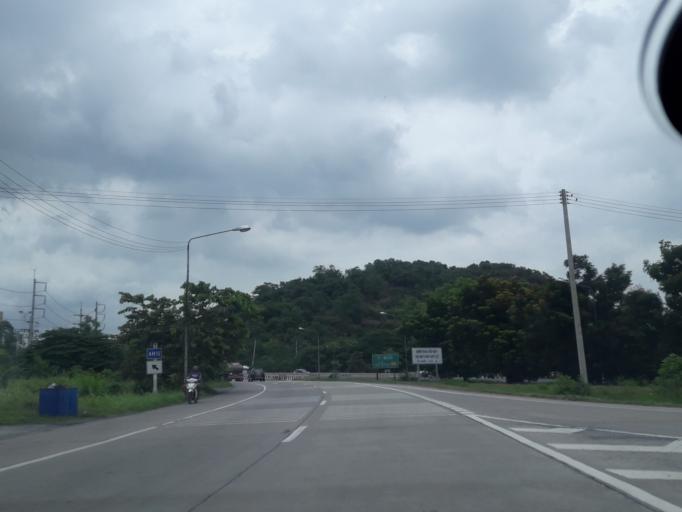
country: TH
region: Sara Buri
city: Saraburi
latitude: 14.5425
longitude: 100.9539
